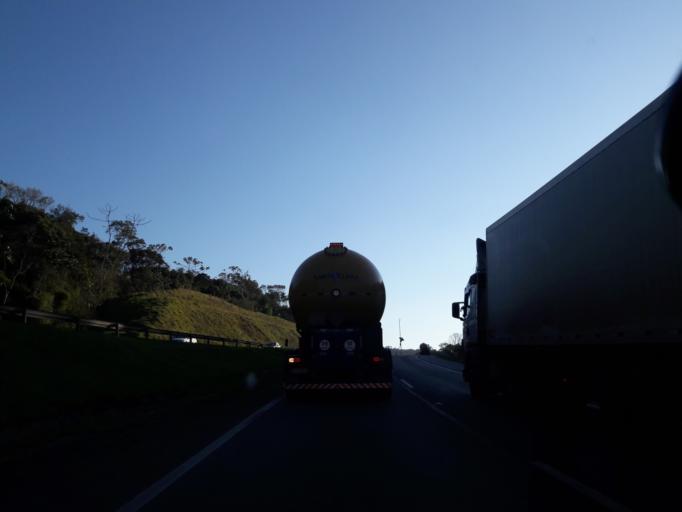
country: BR
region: Sao Paulo
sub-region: Juquitiba
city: Juquitiba
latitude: -23.9588
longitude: -47.1163
